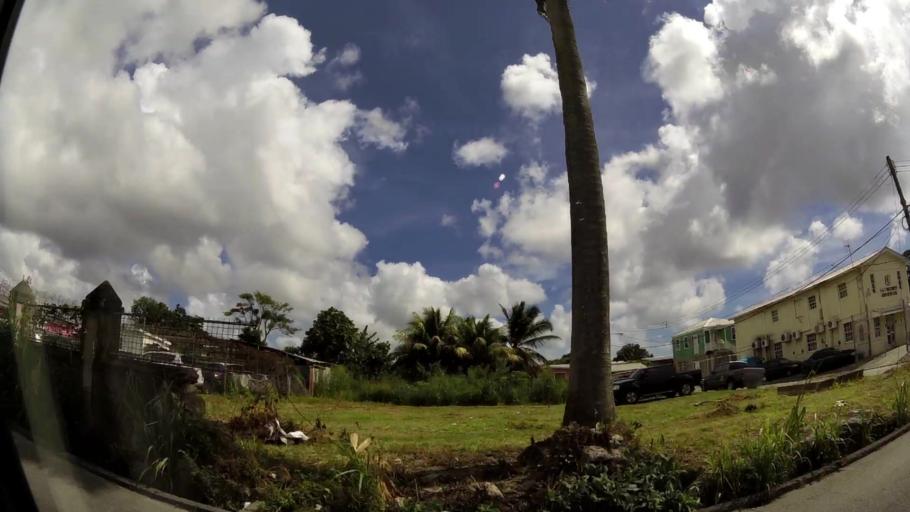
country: BB
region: Saint Michael
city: Bridgetown
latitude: 13.1113
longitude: -59.6154
